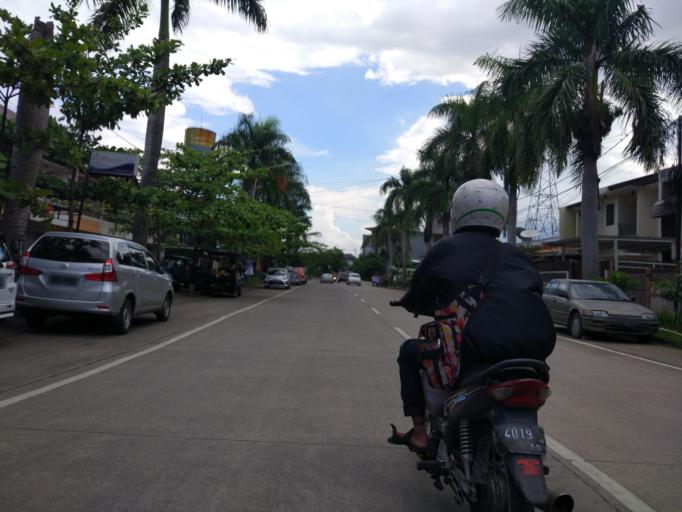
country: ID
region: West Java
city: Bandung
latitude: -6.9218
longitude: 107.6703
